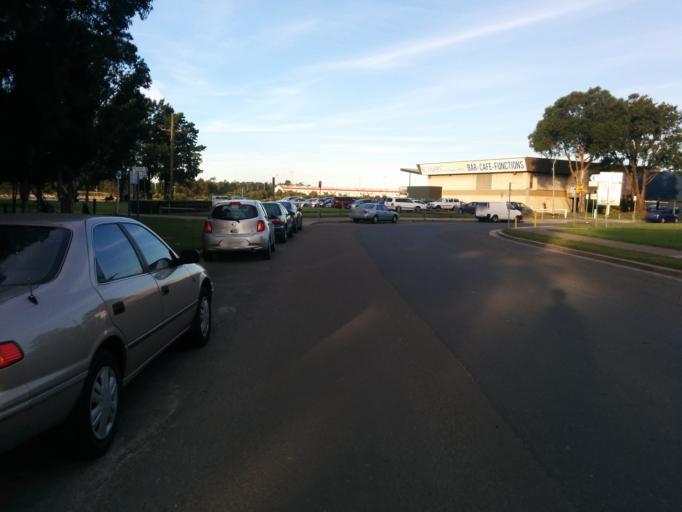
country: AU
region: New South Wales
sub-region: Rockdale
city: Arncliffe
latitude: -33.9335
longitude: 151.1573
